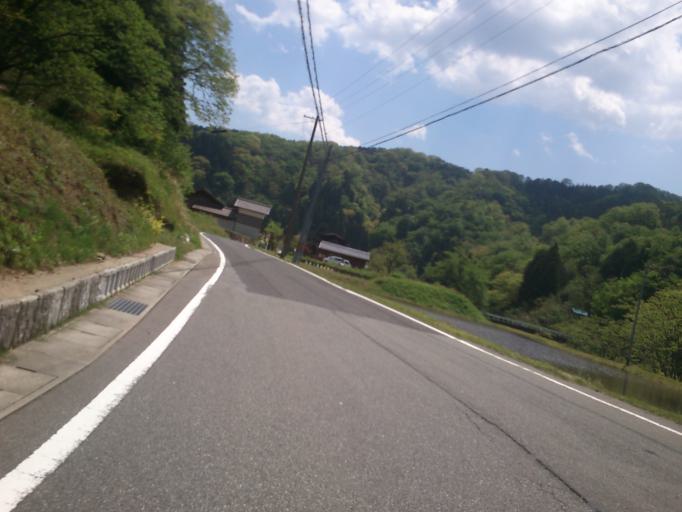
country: JP
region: Kyoto
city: Miyazu
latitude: 35.6870
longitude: 135.1509
